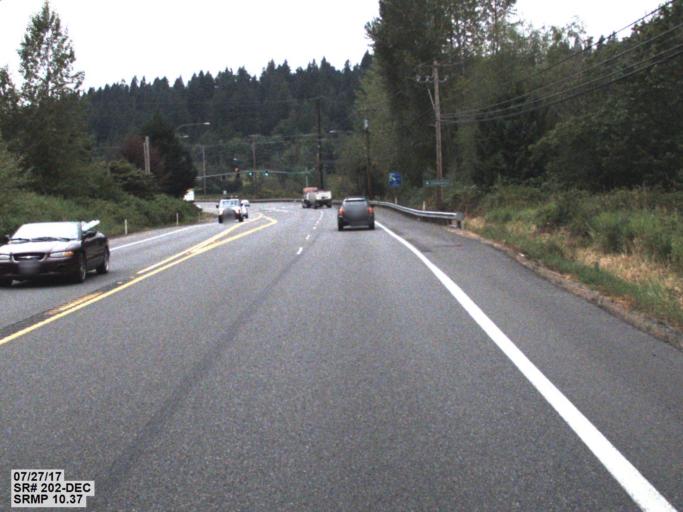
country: US
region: Washington
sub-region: King County
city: Sammamish
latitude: 47.6560
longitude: -122.0605
